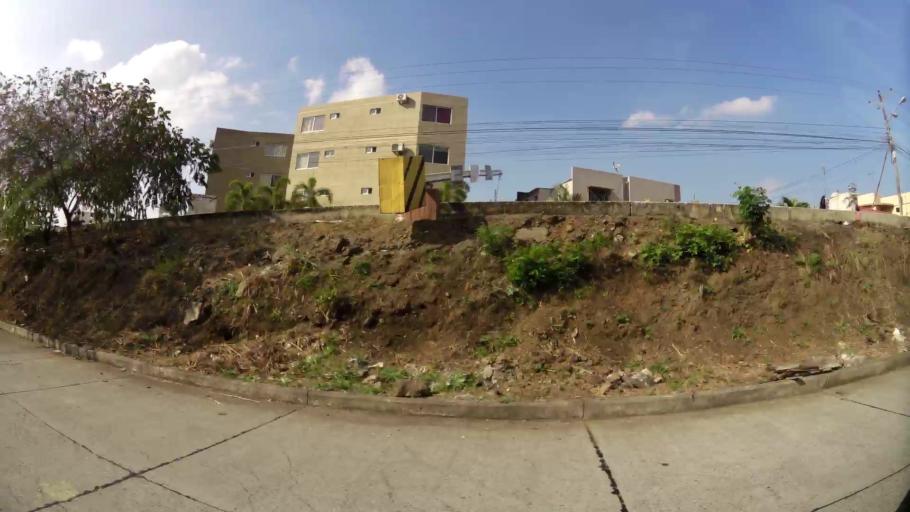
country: EC
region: Guayas
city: Guayaquil
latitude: -2.1346
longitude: -79.9258
